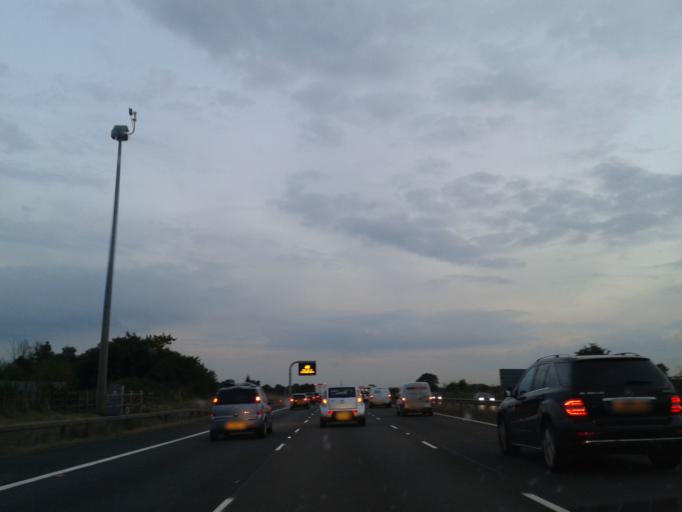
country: GB
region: England
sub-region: Oxfordshire
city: Bicester
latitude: 51.9394
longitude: -1.2020
